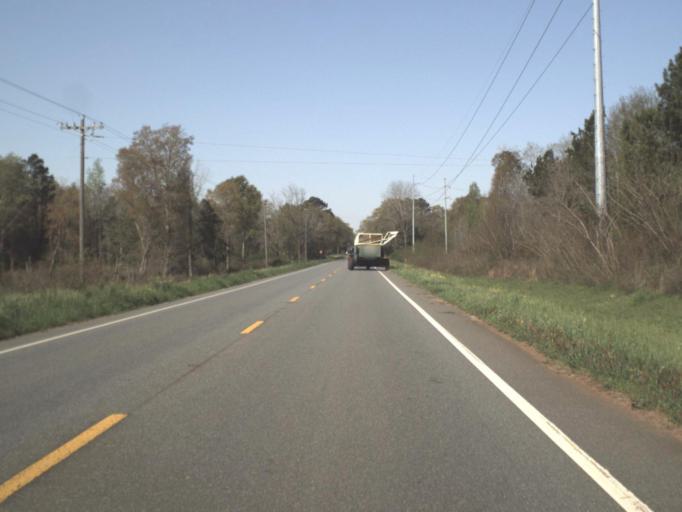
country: US
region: Alabama
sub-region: Houston County
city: Cottonwood
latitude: 30.9482
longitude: -85.3685
